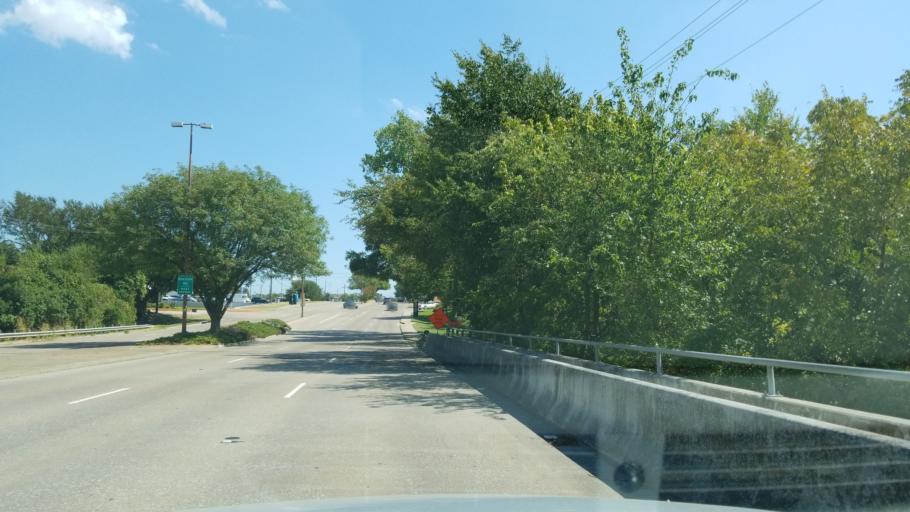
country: US
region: Texas
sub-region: Dallas County
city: Addison
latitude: 32.9540
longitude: -96.8083
